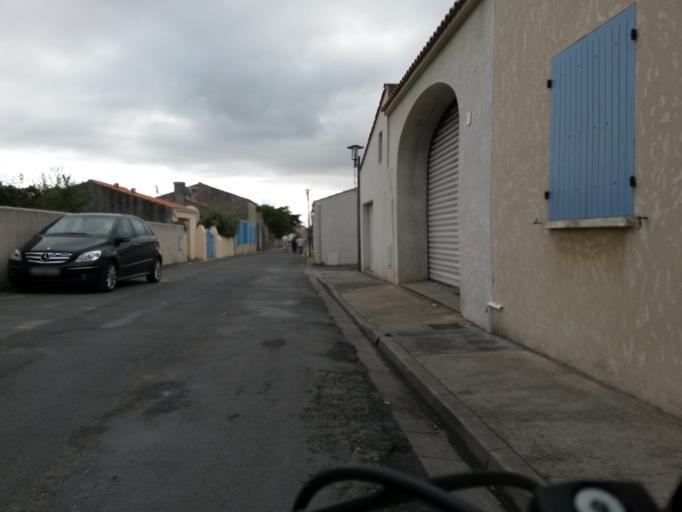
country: FR
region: Poitou-Charentes
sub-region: Departement de la Charente-Maritime
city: Dolus-d'Oleron
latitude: 45.9182
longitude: -1.3332
